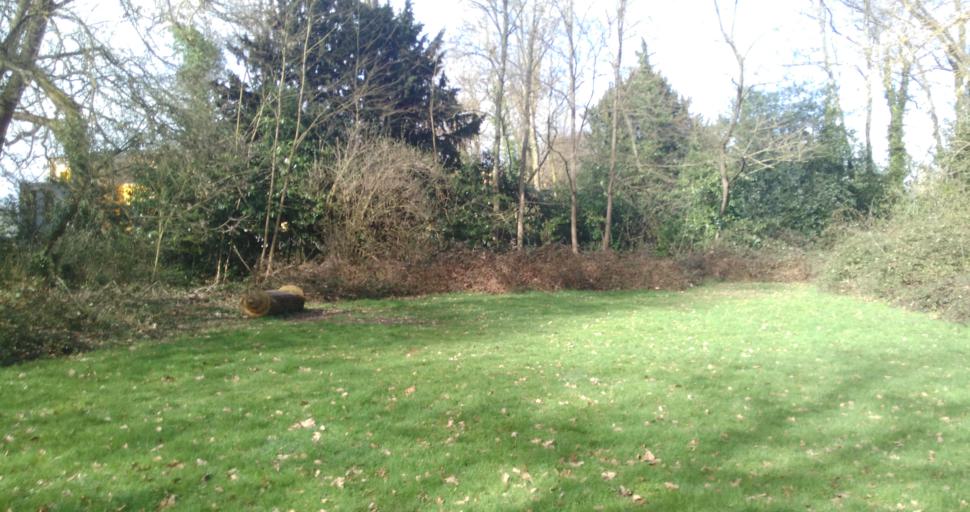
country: FR
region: Brittany
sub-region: Departement d'Ille-et-Vilaine
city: Chantepie
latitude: 48.0928
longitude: -1.6435
